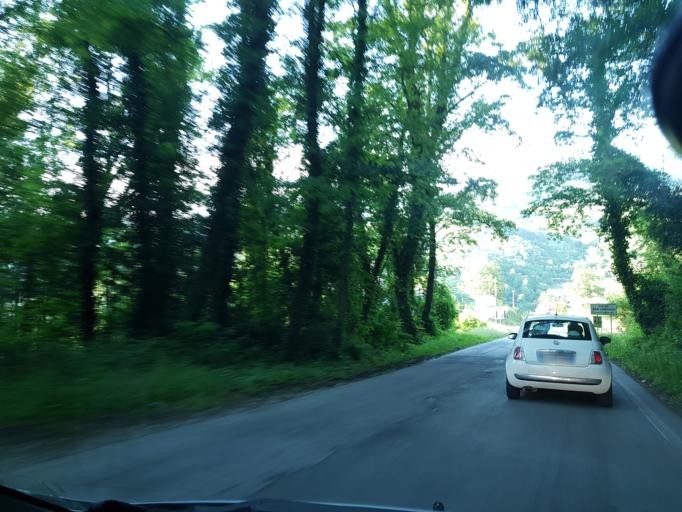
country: IT
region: Tuscany
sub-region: Provincia di Massa-Carrara
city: Casola in Lunigiana
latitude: 44.1907
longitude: 10.1943
